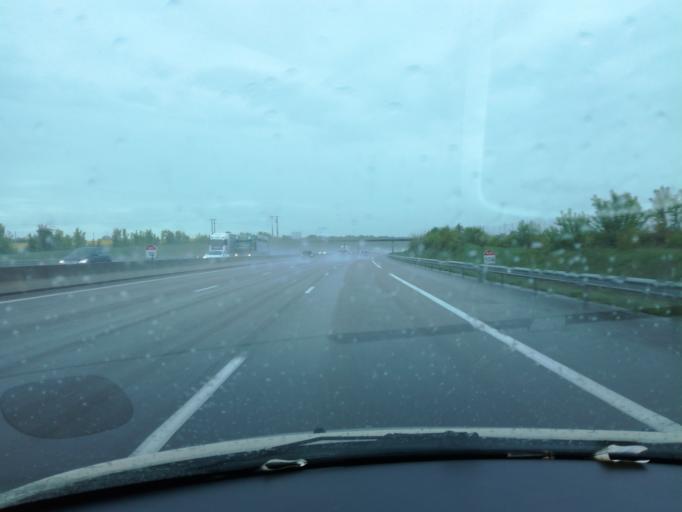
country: FR
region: Champagne-Ardenne
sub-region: Departement de la Haute-Marne
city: Langres
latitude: 47.8411
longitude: 5.2317
